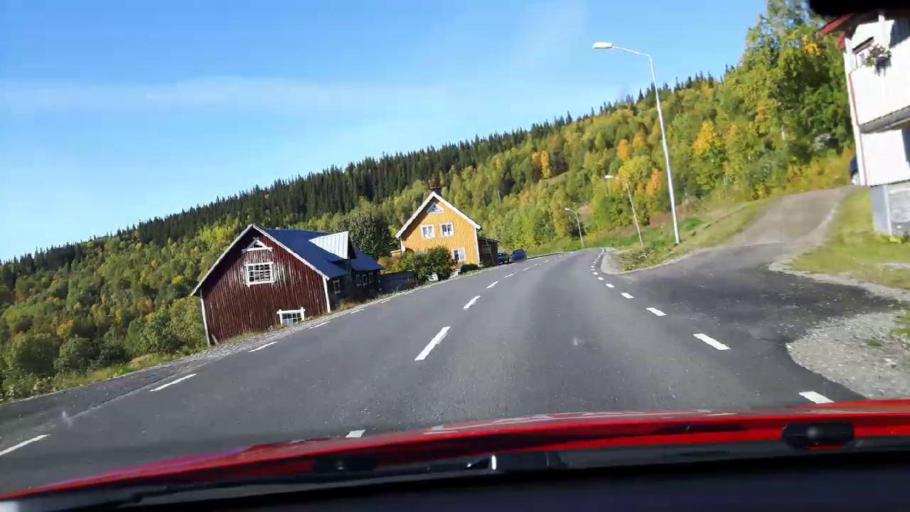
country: NO
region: Nord-Trondelag
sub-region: Royrvik
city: Royrvik
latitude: 64.8359
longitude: 14.1072
